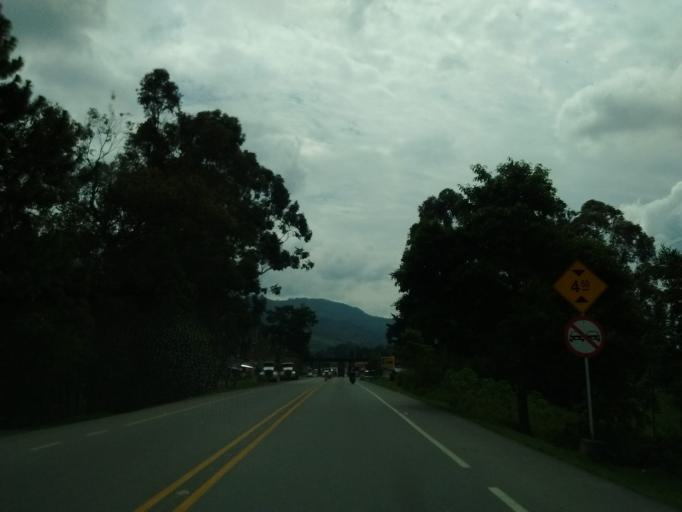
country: CO
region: Cauca
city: Cajibio
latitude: 2.7036
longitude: -76.5381
